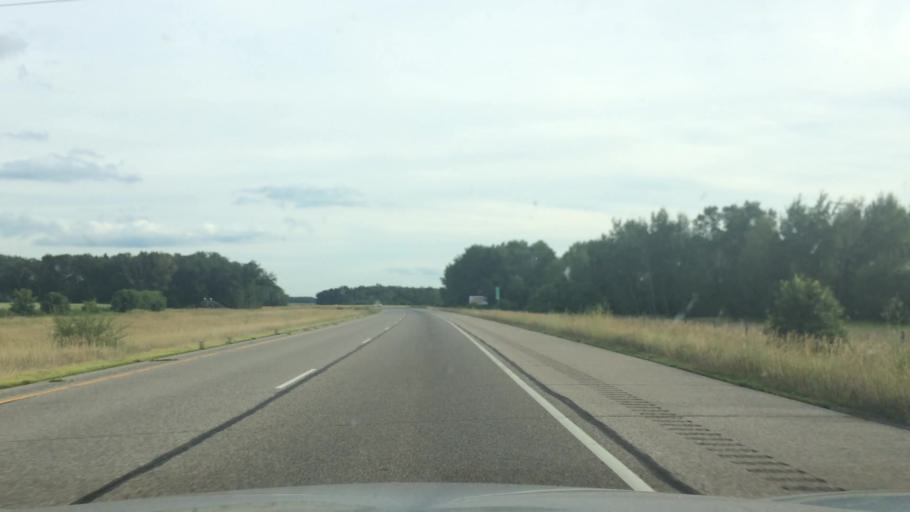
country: US
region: Wisconsin
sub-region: Waushara County
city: Wautoma
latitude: 44.1752
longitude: -89.5309
